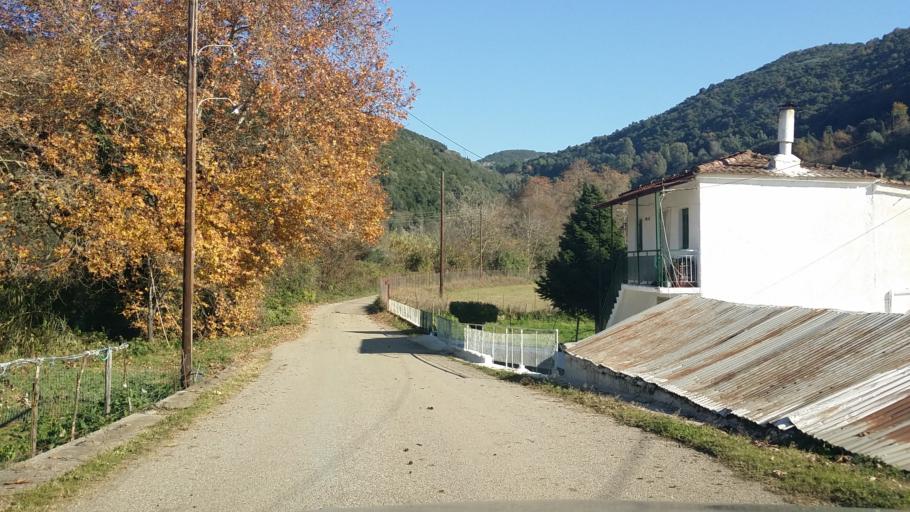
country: GR
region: West Greece
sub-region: Nomos Aitolias kai Akarnanias
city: Krikellos
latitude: 38.9609
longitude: 21.1911
